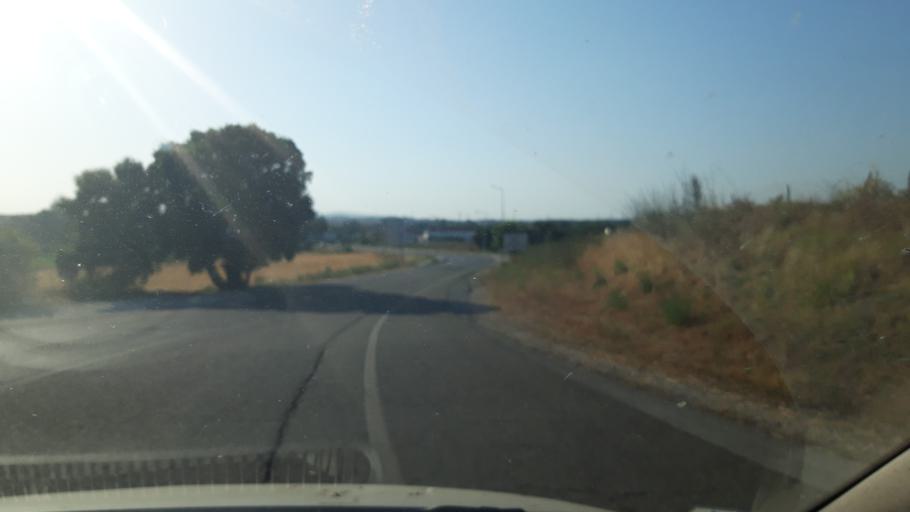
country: PT
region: Santarem
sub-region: Entroncamento
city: Entroncamento
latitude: 39.4630
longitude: -8.4577
